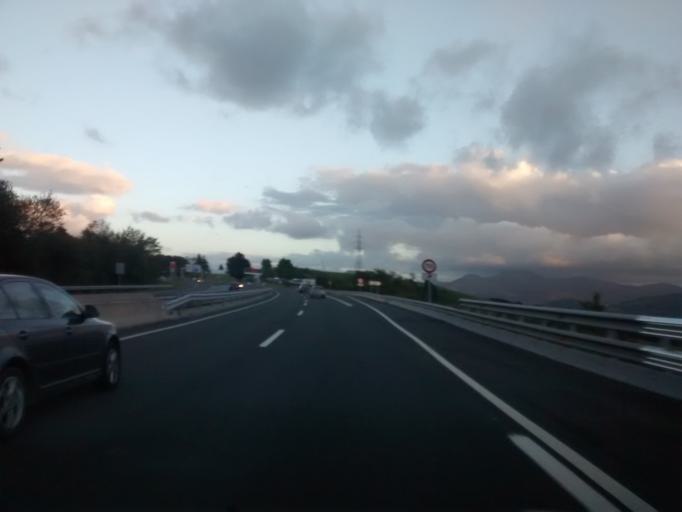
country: ES
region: Basque Country
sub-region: Provincia de Guipuzcoa
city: Usurbil
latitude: 43.2879
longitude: -2.0355
